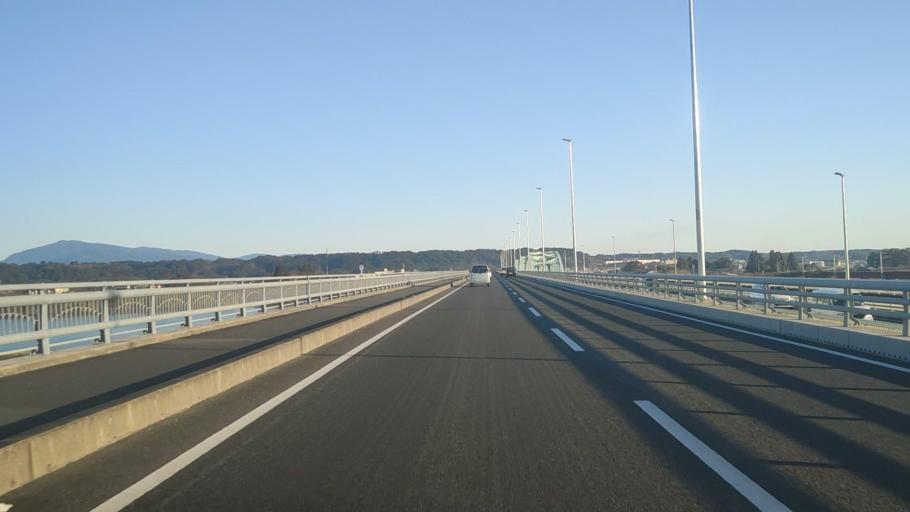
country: JP
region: Miyazaki
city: Tsuma
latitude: 32.0467
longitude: 131.4723
